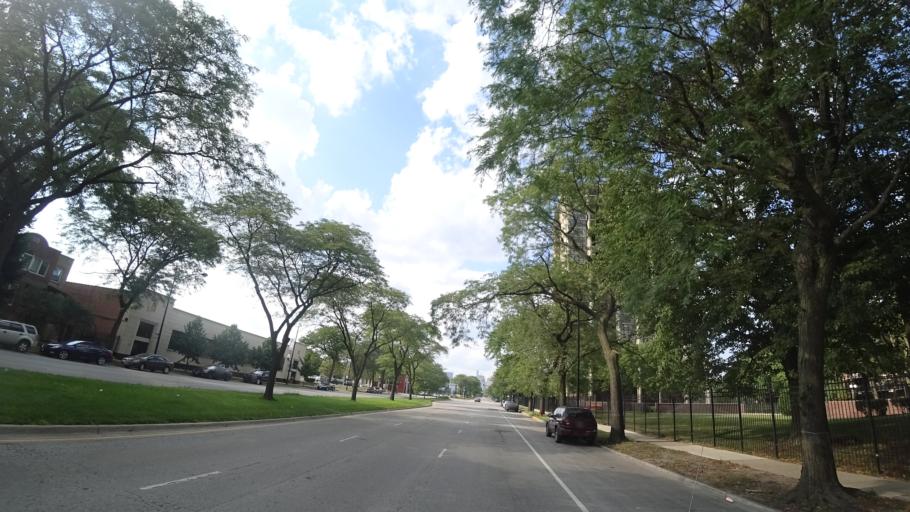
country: US
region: Illinois
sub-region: Cook County
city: Chicago
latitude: 41.8407
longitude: -87.6233
